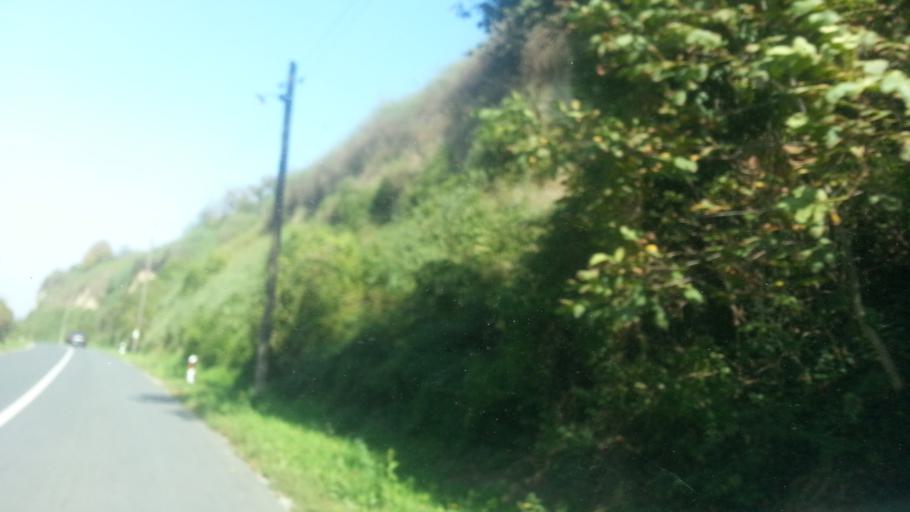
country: RS
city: Novi Slankamen
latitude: 45.1371
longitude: 20.2539
